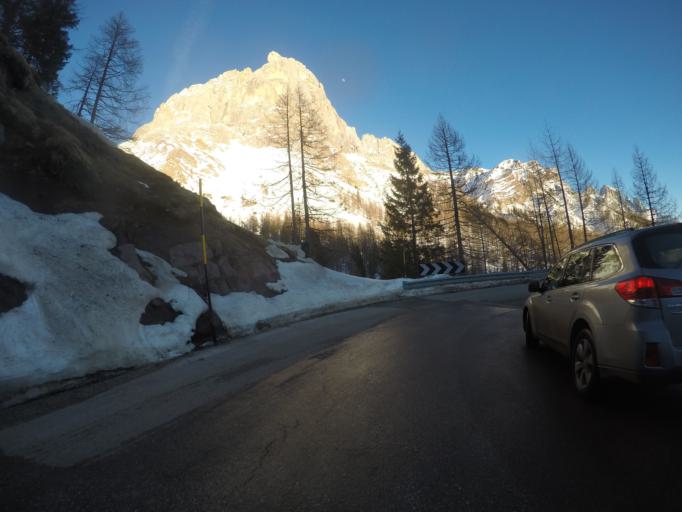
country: IT
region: Veneto
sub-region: Provincia di Belluno
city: Falcade Alto
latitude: 46.2850
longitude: 11.8005
